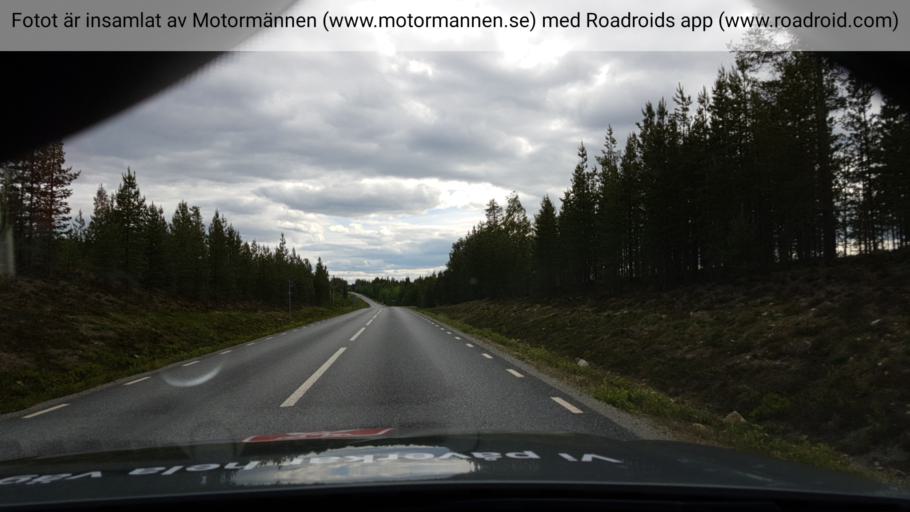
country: SE
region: Jaemtland
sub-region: Stroemsunds Kommun
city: Stroemsund
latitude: 63.9744
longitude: 15.4886
